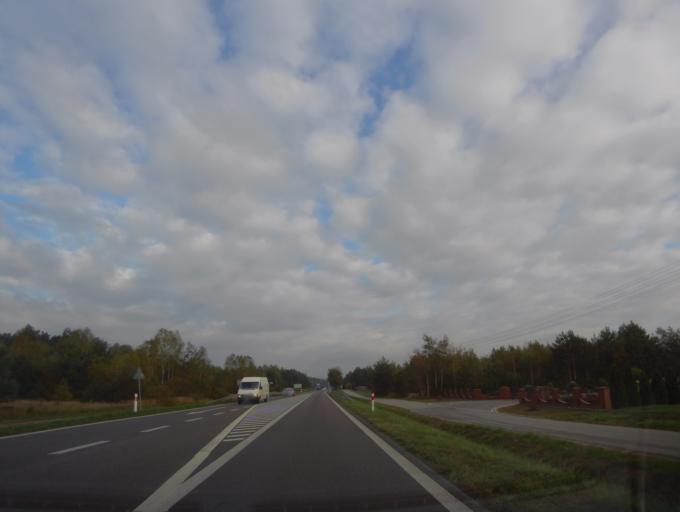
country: PL
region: Lublin Voivodeship
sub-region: Powiat bilgorajski
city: Bilgoraj
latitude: 50.5787
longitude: 22.6859
